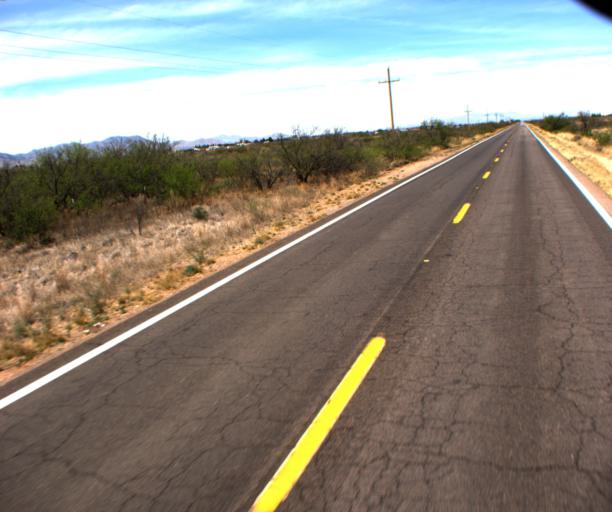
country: US
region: Arizona
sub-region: Cochise County
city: Tombstone
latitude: 31.9163
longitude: -109.8189
